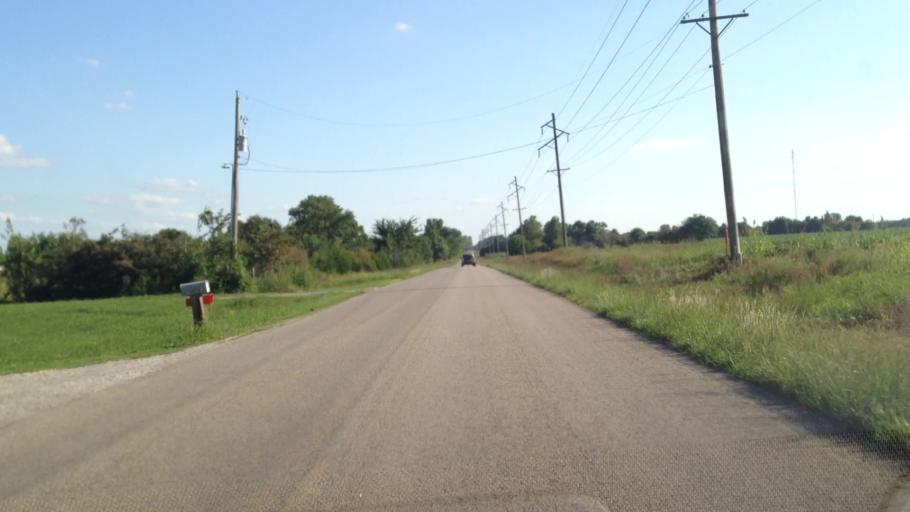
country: US
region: Kansas
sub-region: Crawford County
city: Frontenac
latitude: 37.4624
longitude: -94.6308
